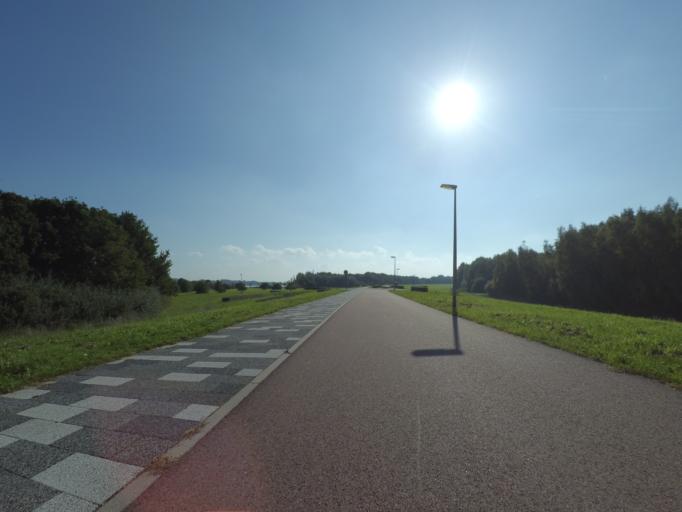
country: NL
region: Flevoland
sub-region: Gemeente Zeewolde
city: Zeewolde
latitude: 52.3220
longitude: 5.5493
